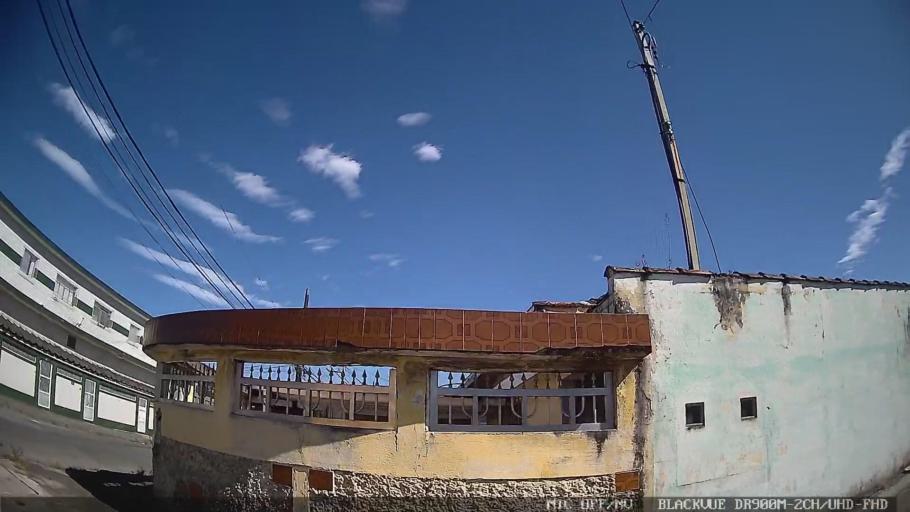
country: BR
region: Sao Paulo
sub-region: Santos
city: Santos
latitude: -23.9442
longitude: -46.2948
